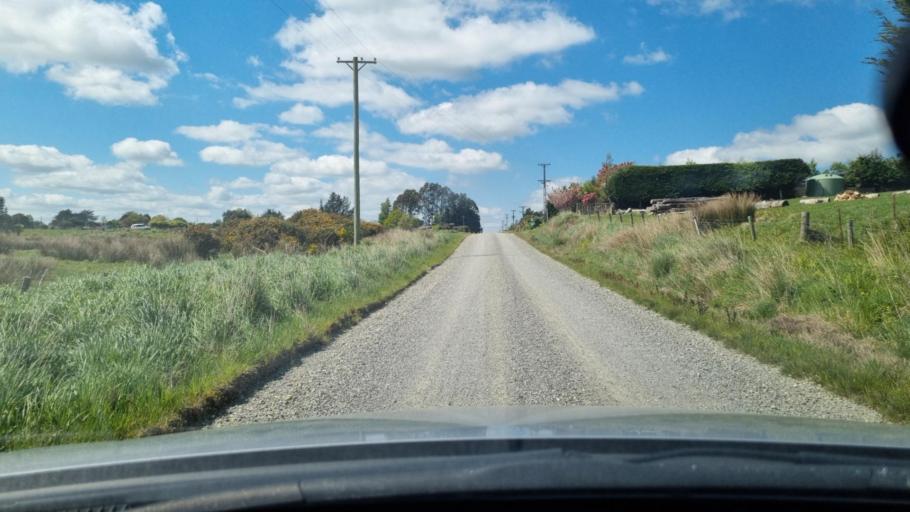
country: NZ
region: Southland
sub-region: Invercargill City
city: Invercargill
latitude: -46.3222
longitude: 168.3421
